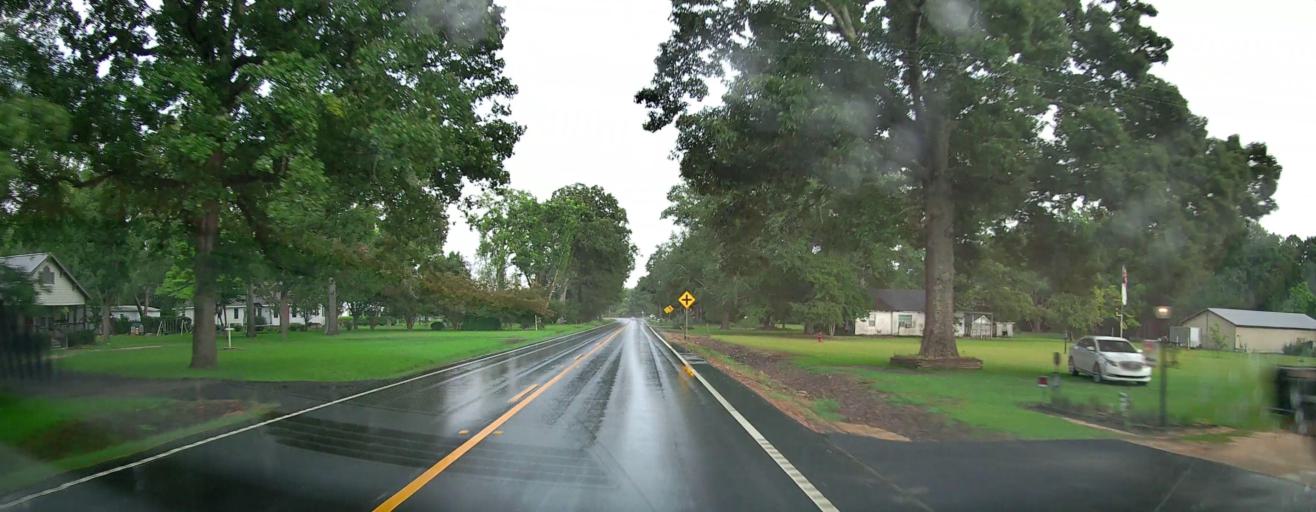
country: US
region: Georgia
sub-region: Dodge County
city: Chester
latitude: 32.5570
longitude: -83.1496
